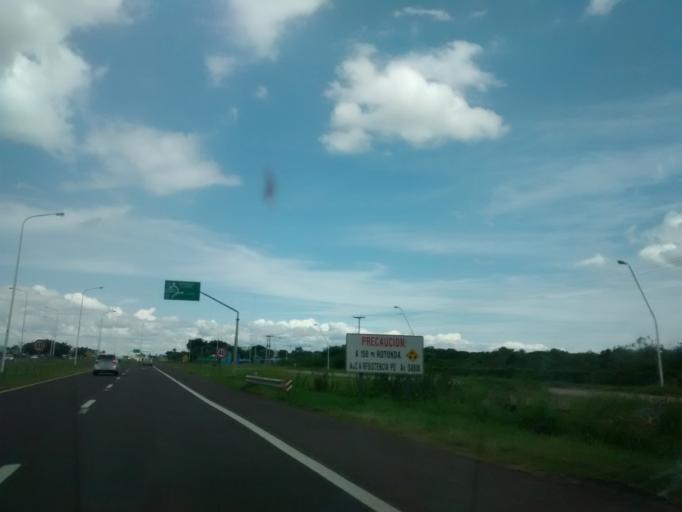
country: AR
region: Chaco
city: Resistencia
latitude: -27.4139
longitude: -58.9710
